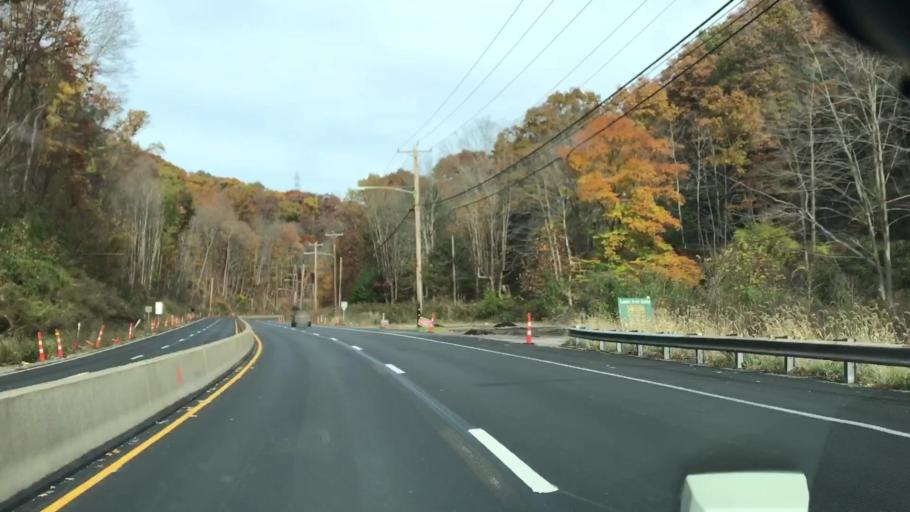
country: US
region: Pennsylvania
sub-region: Allegheny County
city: Carnot-Moon
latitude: 40.5297
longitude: -80.2049
